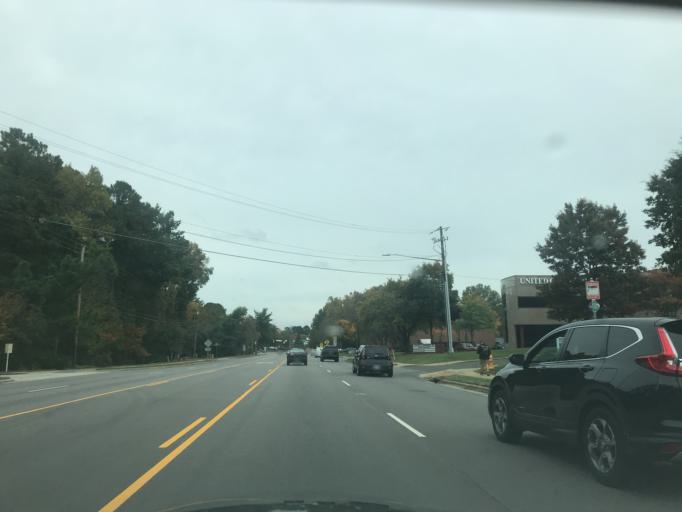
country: US
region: North Carolina
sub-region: Wake County
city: West Raleigh
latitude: 35.8637
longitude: -78.6200
